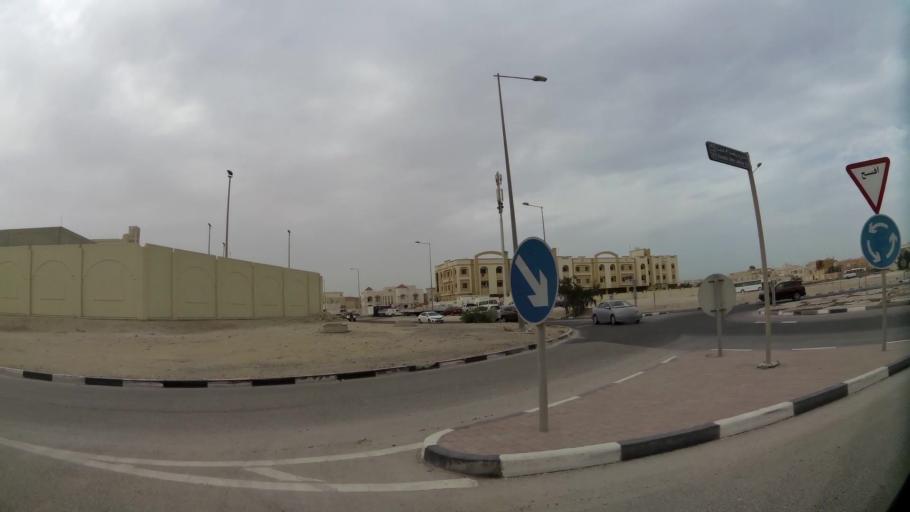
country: QA
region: Baladiyat ar Rayyan
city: Ar Rayyan
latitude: 25.3421
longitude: 51.4701
